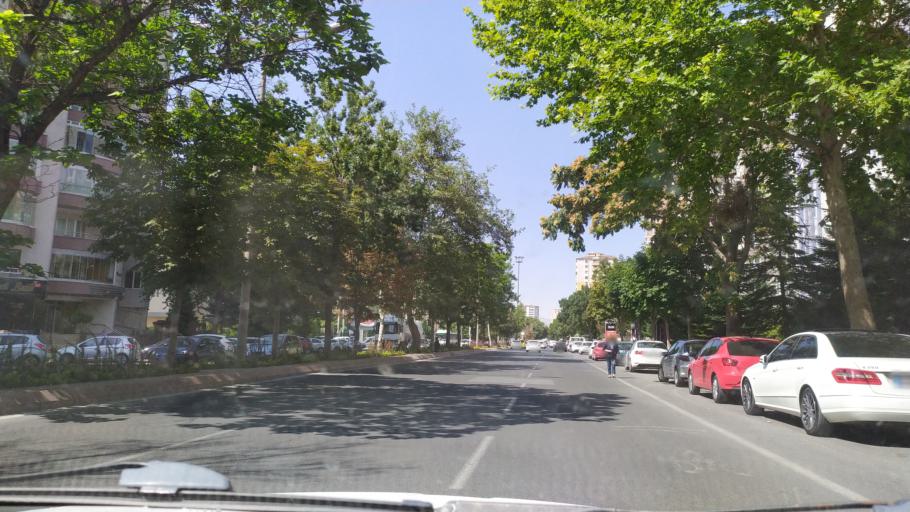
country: TR
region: Kayseri
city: Kayseri
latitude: 38.7262
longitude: 35.5197
